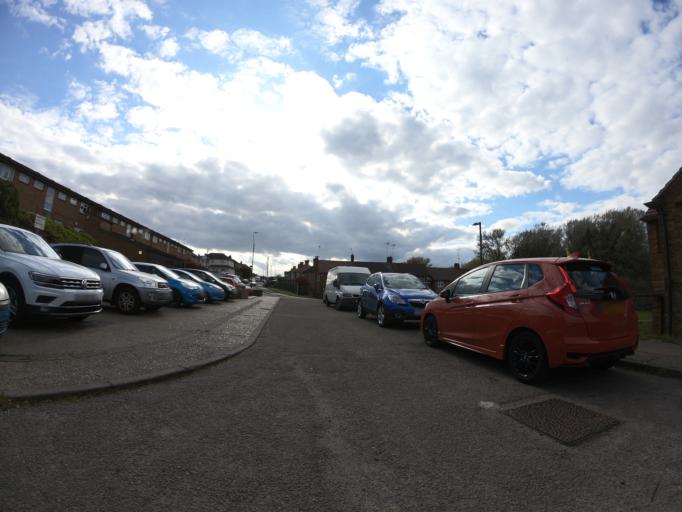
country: GB
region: England
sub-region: Greater London
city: Belvedere
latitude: 51.4798
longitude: 0.1494
